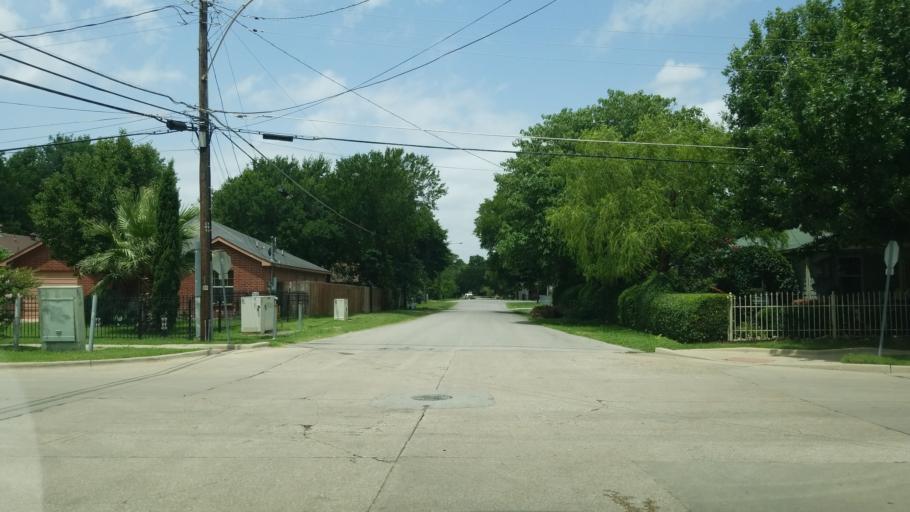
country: US
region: Texas
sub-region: Dallas County
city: Irving
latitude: 32.7850
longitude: -96.9056
